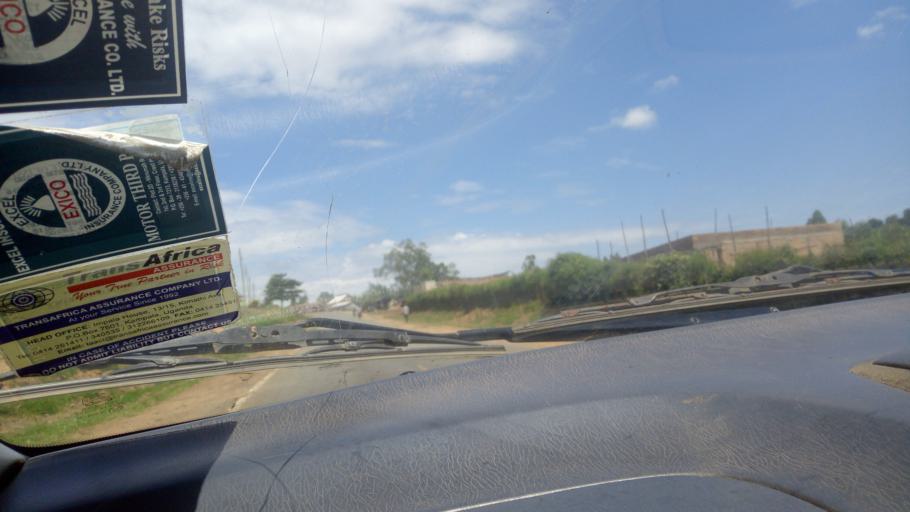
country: UG
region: Western Region
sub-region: Buhweju District
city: Buhweju
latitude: -0.2751
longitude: 30.5640
